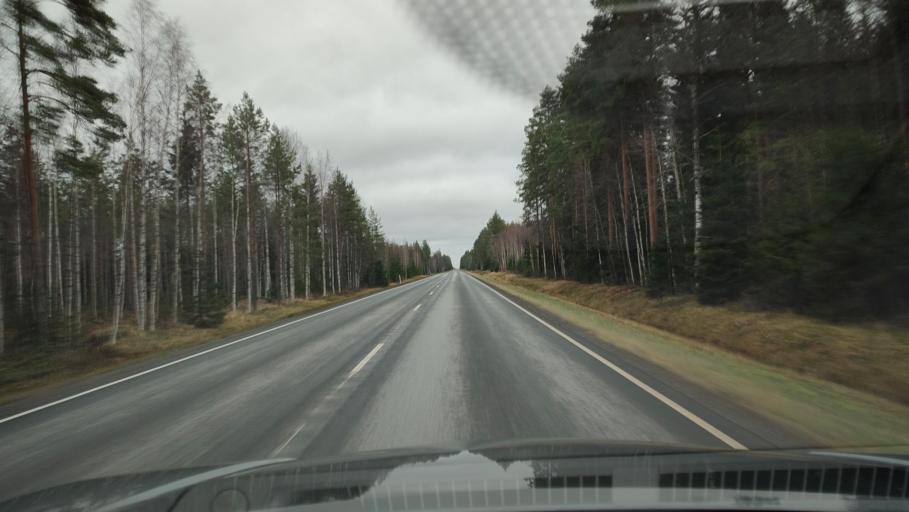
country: FI
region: Southern Ostrobothnia
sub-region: Seinaejoki
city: Kurikka
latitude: 62.5232
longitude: 22.3206
